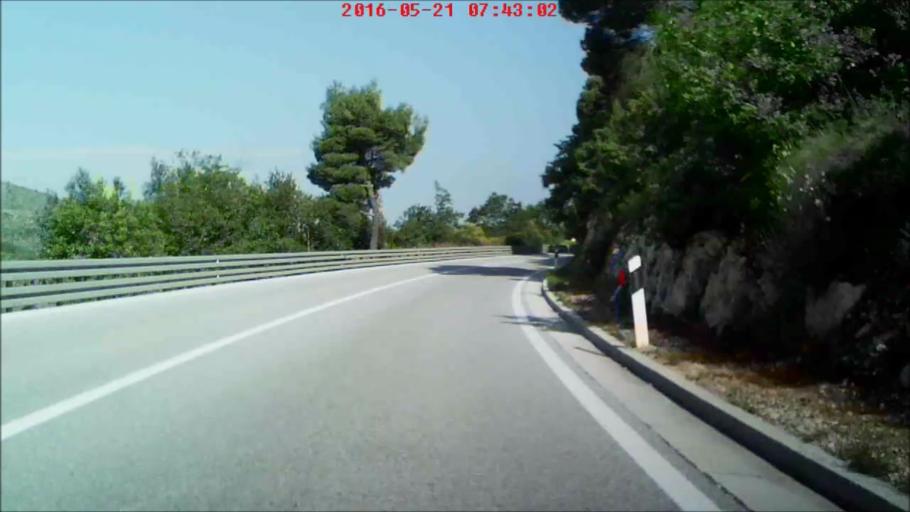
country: HR
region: Dubrovacko-Neretvanska
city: Podgora
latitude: 42.8109
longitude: 17.7948
